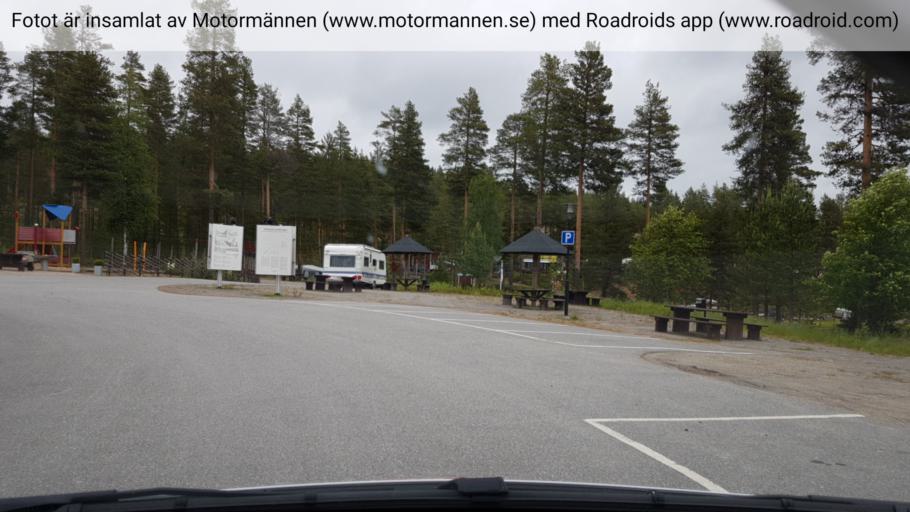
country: SE
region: Vaesterbotten
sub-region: Vindelns Kommun
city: Vindeln
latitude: 64.0579
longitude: 19.6485
